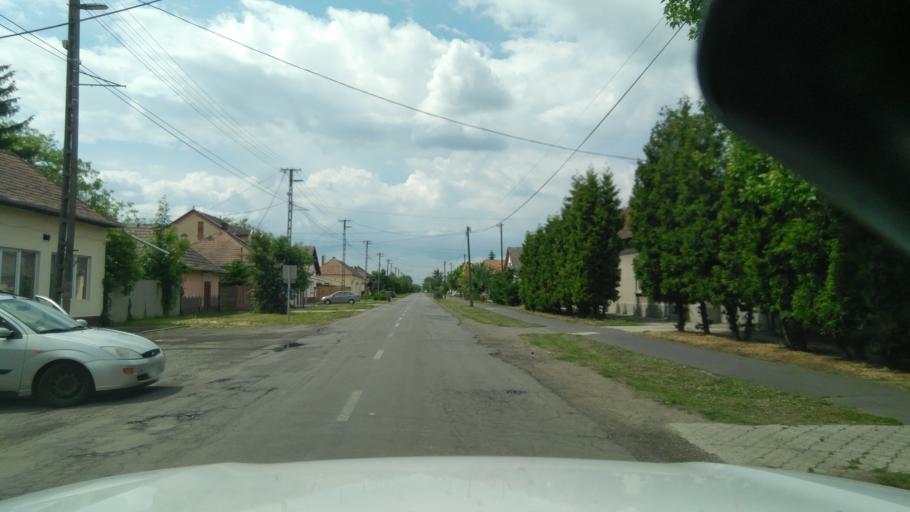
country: HU
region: Bekes
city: Magyarbanhegyes
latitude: 46.4572
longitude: 20.9635
